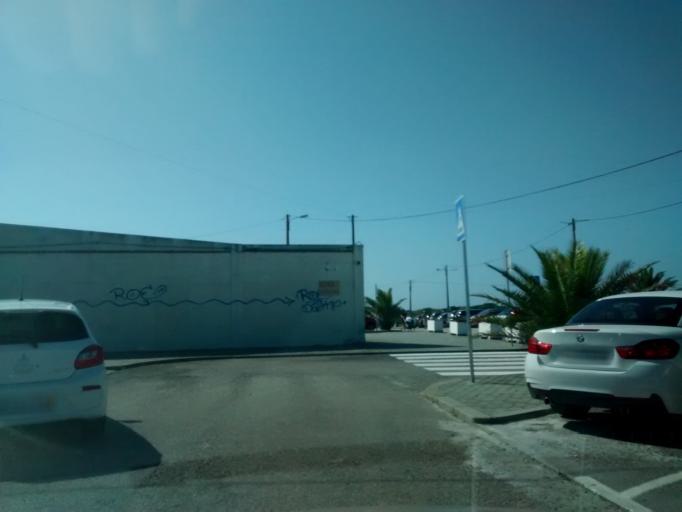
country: PT
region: Aveiro
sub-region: Ilhavo
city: Gafanha da Nazare
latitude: 40.6683
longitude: -8.7421
